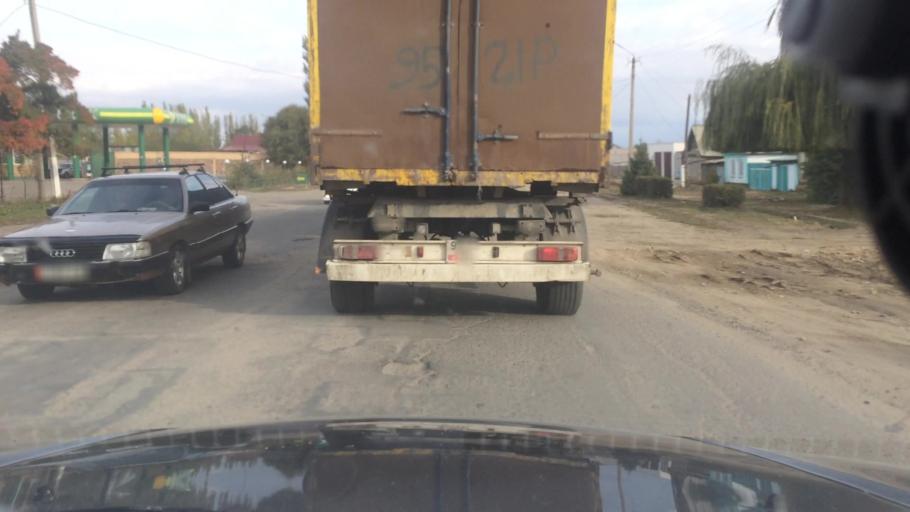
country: KG
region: Ysyk-Koel
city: Karakol
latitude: 42.5174
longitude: 78.3858
